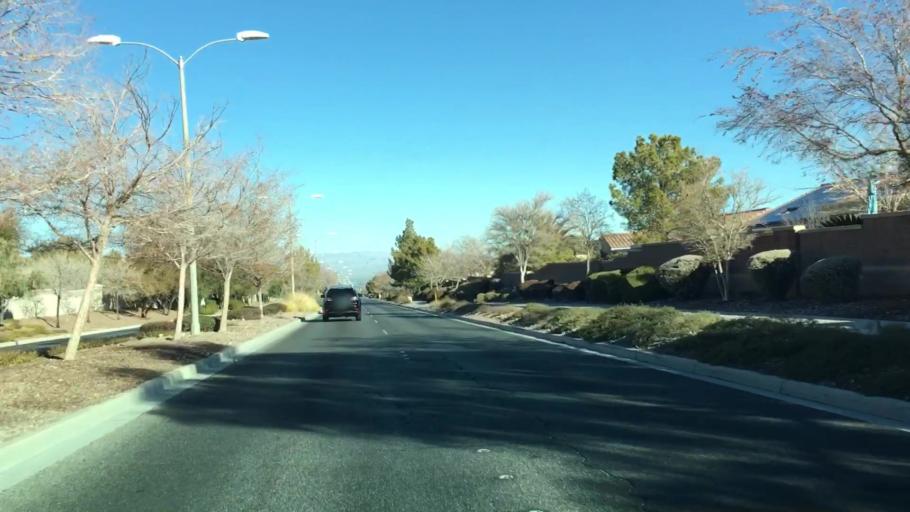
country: US
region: Nevada
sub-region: Clark County
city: Whitney
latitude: 35.9705
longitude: -115.1009
